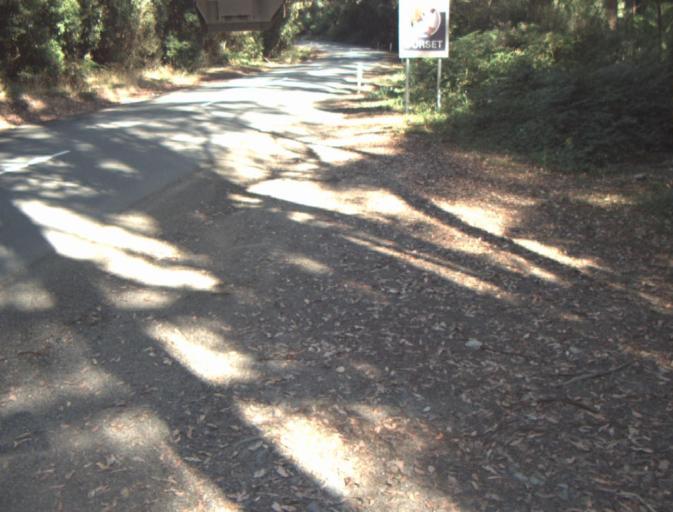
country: AU
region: Tasmania
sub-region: Dorset
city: Scottsdale
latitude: -41.2678
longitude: 147.3831
